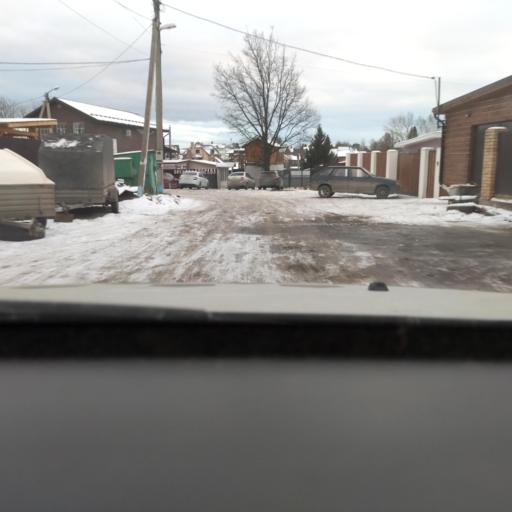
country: RU
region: Perm
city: Perm
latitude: 58.0487
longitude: 56.3493
